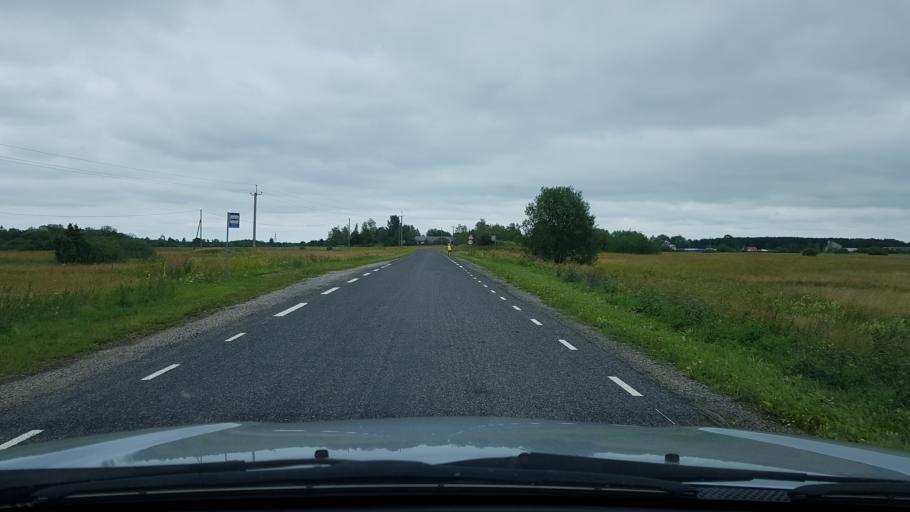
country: EE
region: Ida-Virumaa
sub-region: Narva linn
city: Narva
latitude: 59.3811
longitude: 28.1292
